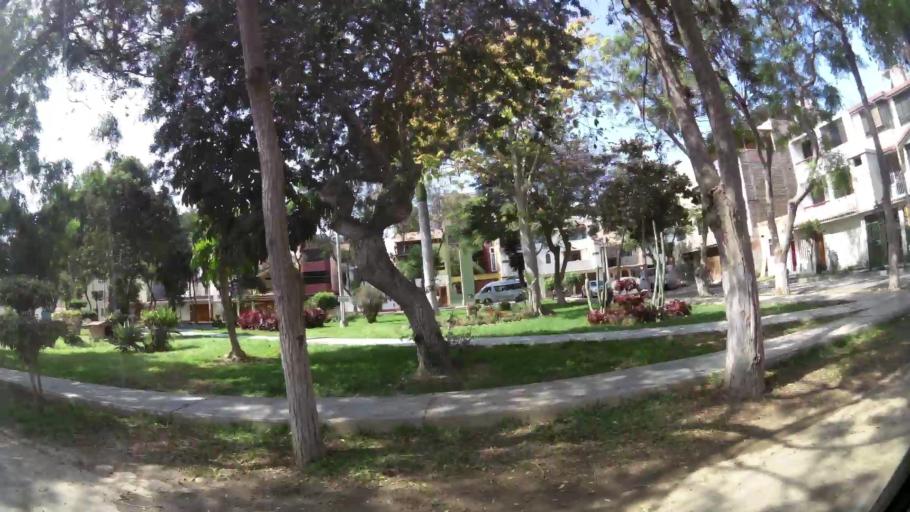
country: PE
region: La Libertad
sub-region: Provincia de Trujillo
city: Buenos Aires
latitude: -8.1314
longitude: -79.0457
